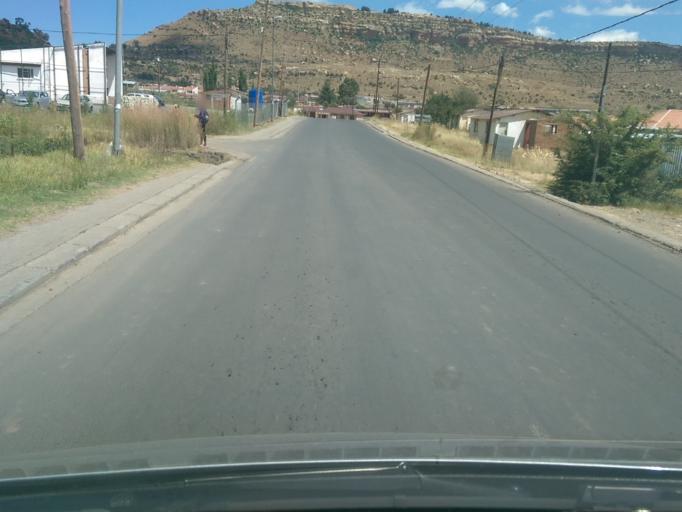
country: LS
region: Maseru
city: Maseru
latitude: -29.3256
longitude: 27.4864
